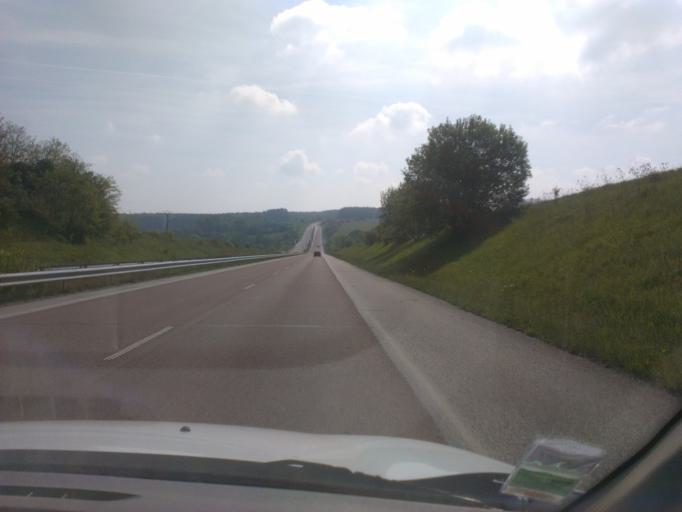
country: FR
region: Lorraine
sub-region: Departement des Vosges
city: Uxegney
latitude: 48.2044
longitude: 6.3709
